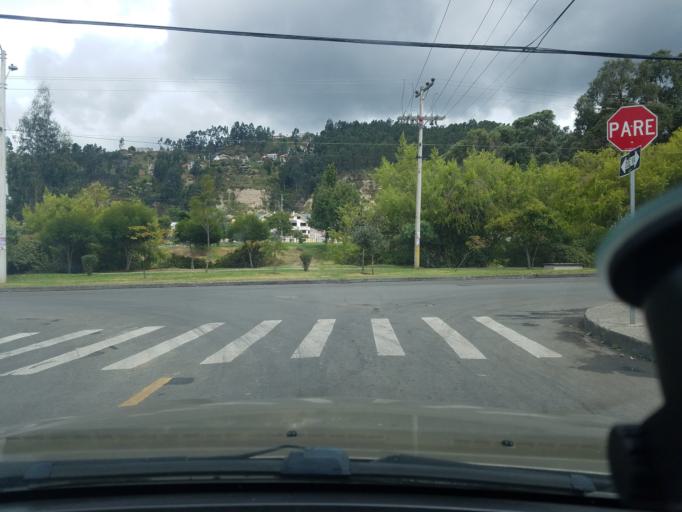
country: EC
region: Azuay
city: Cuenca
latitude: -2.9071
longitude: -78.9846
